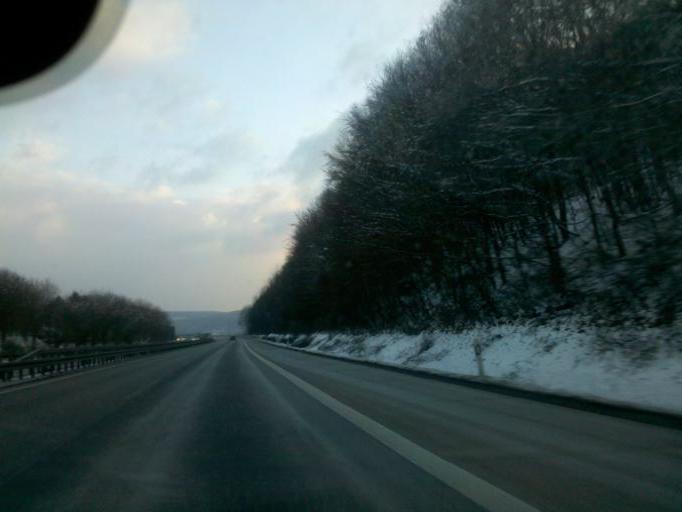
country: DE
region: North Rhine-Westphalia
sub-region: Regierungsbezirk Arnsberg
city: Siegen
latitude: 50.8553
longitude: 7.9862
